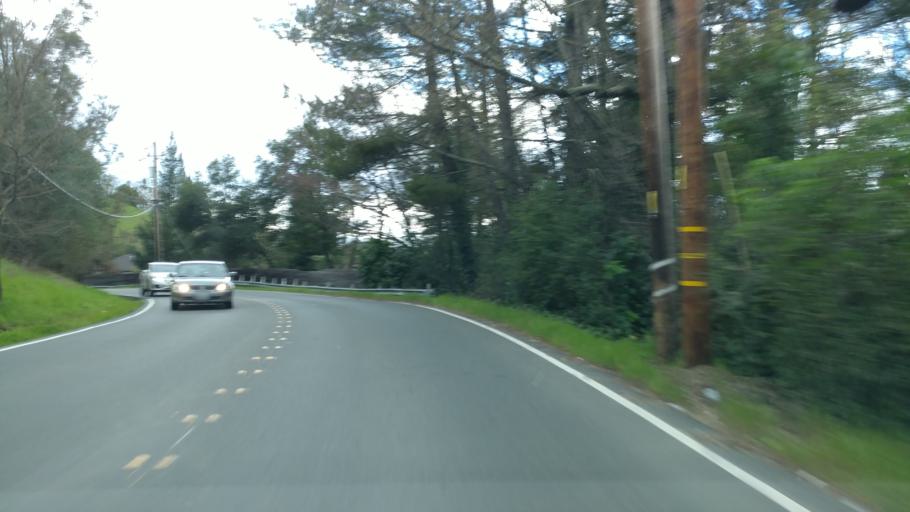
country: US
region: California
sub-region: Contra Costa County
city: Diablo
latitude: 37.8335
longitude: -121.9603
